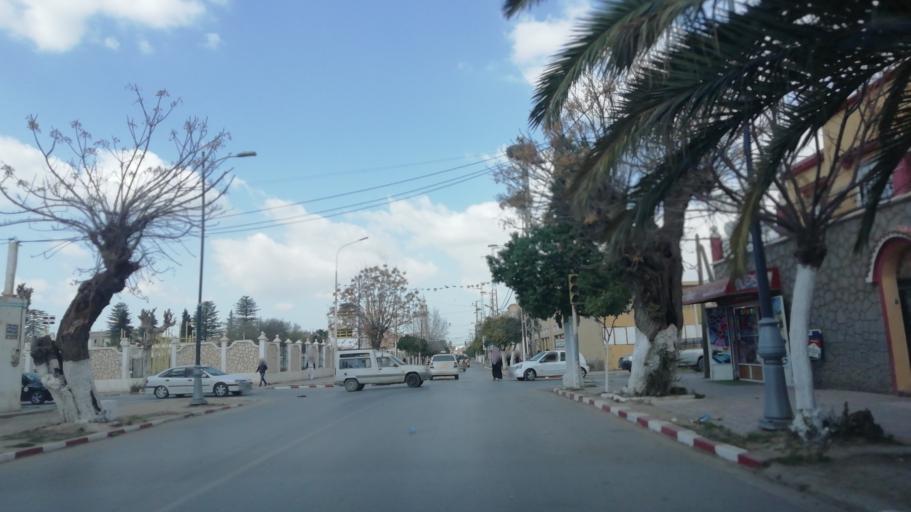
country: DZ
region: Mascara
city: Mascara
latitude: 35.5851
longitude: 0.0687
